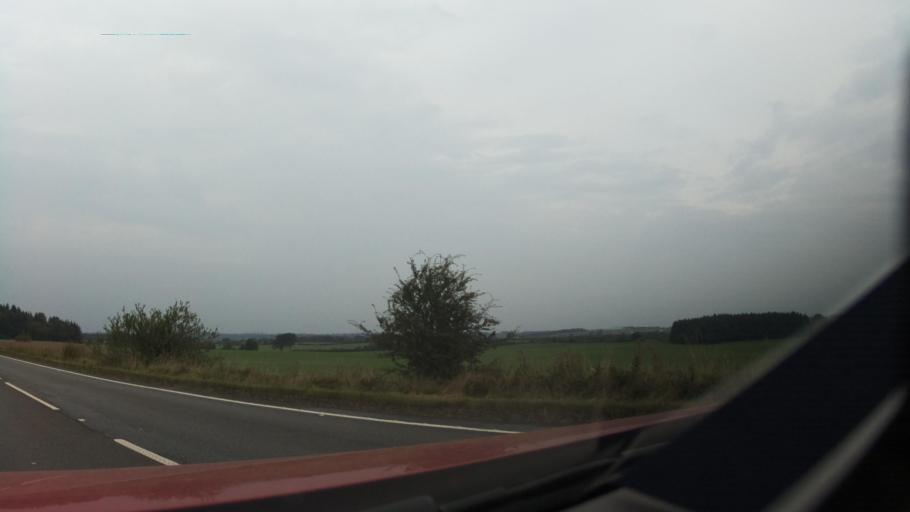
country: GB
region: Scotland
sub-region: Dumfries and Galloway
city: Gretna
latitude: 54.9925
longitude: -3.1210
